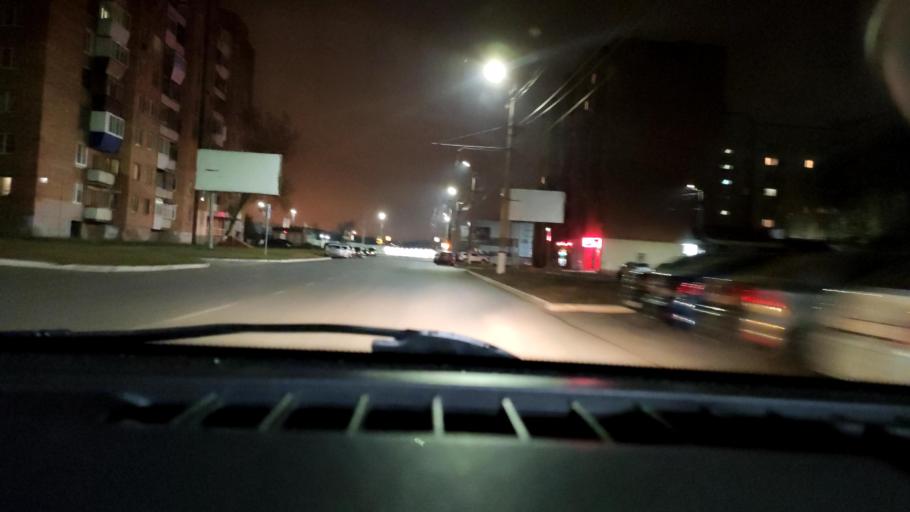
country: RU
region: Samara
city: Novokuybyshevsk
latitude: 53.1094
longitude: 49.9509
